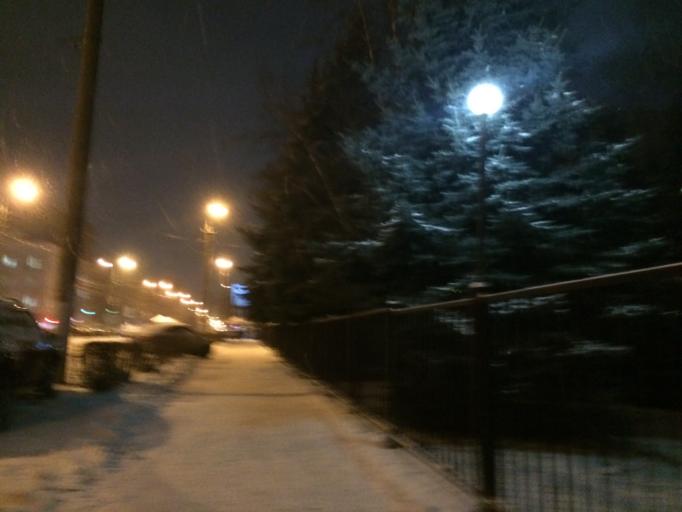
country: RU
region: Tula
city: Tula
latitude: 54.1797
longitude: 37.5986
